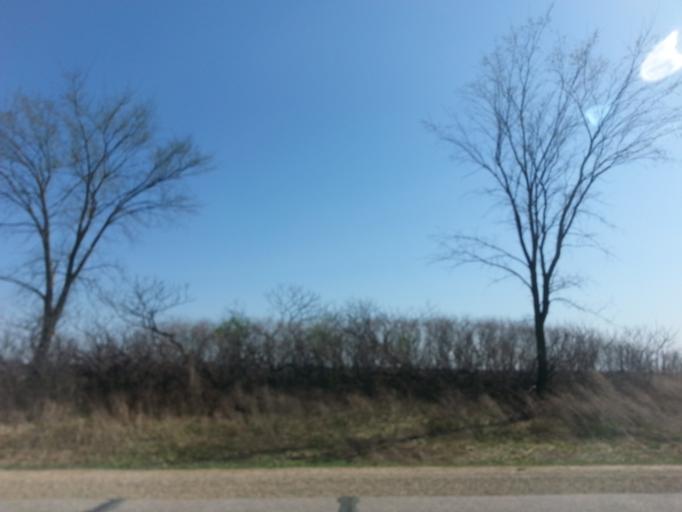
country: US
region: Wisconsin
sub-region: Pepin County
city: Durand
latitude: 44.6404
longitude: -92.1208
